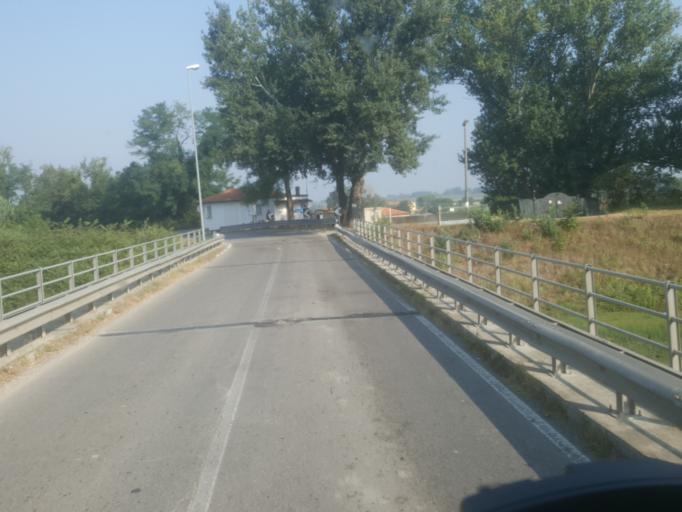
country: IT
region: Emilia-Romagna
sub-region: Provincia di Ravenna
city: Voltana
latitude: 44.5545
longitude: 11.9347
